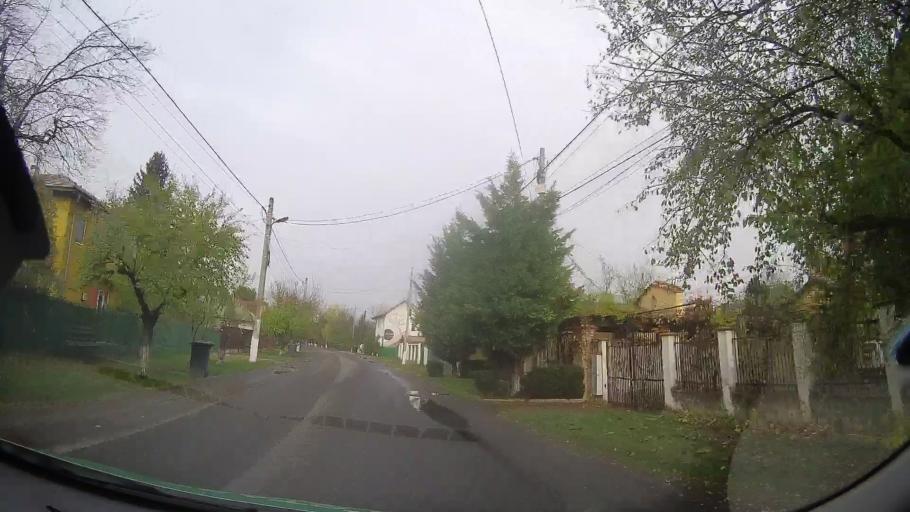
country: RO
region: Ilfov
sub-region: Comuna Snagov
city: Snagov
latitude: 44.7120
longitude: 26.1733
